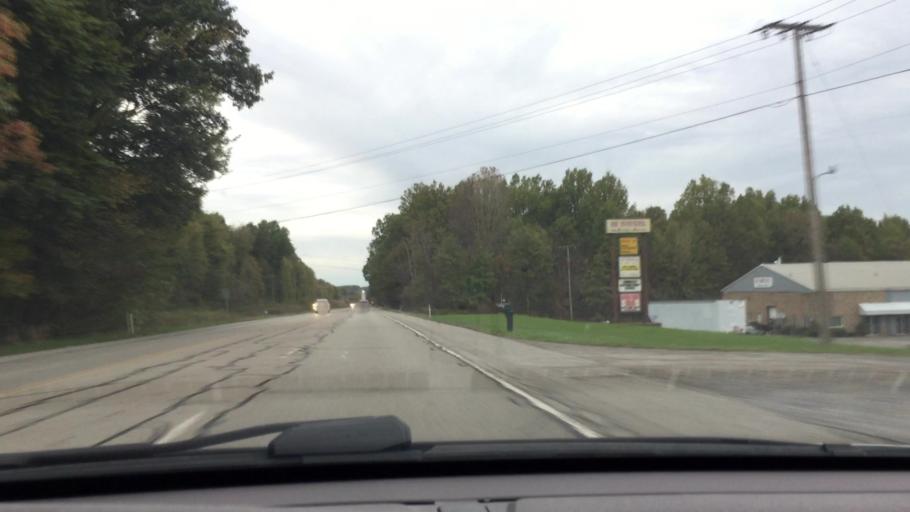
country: US
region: Ohio
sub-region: Mahoning County
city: Lowellville
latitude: 41.0616
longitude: -80.4551
